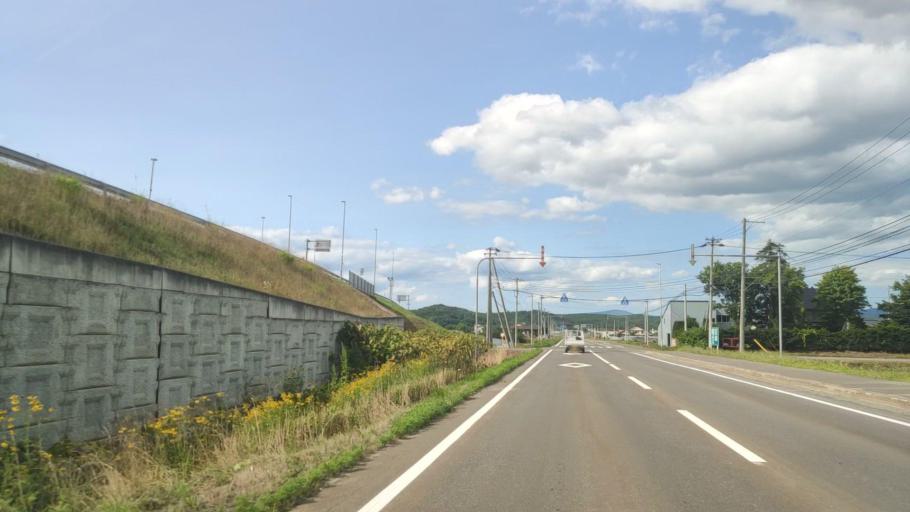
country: JP
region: Hokkaido
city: Nayoro
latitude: 44.3658
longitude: 142.4361
